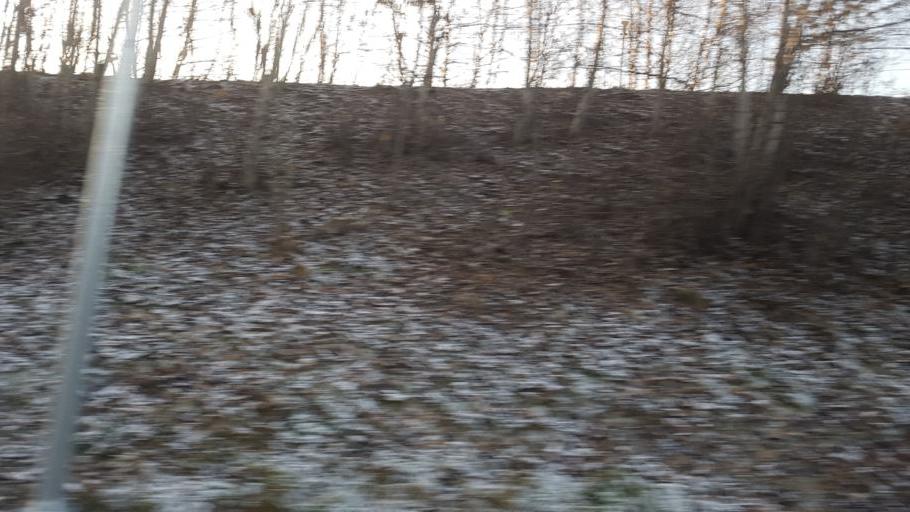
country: NO
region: Sor-Trondelag
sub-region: Melhus
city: Melhus
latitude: 63.3033
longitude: 10.2886
